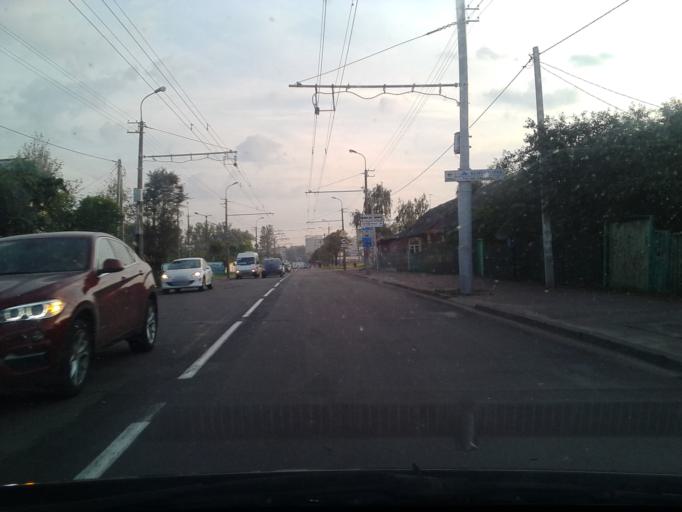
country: BY
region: Minsk
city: Minsk
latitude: 53.9467
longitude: 27.5937
